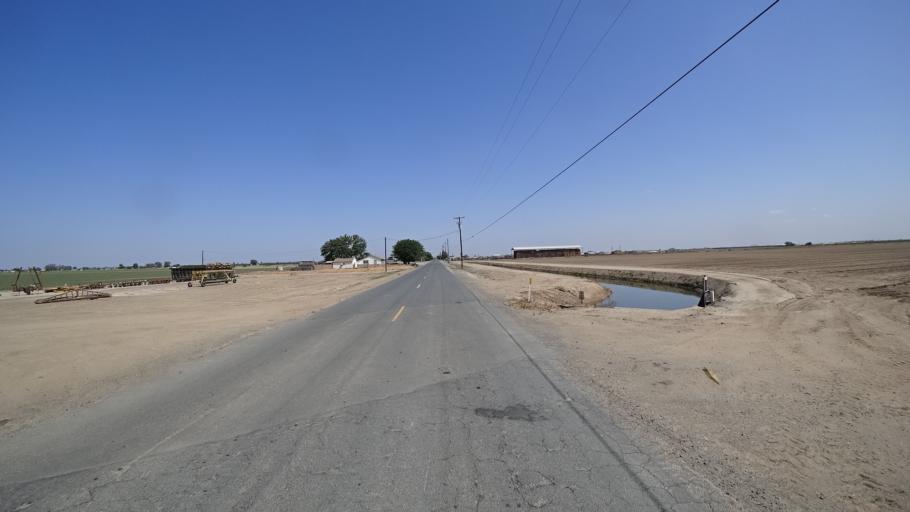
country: US
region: California
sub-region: Kings County
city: Home Garden
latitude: 36.2738
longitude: -119.6190
